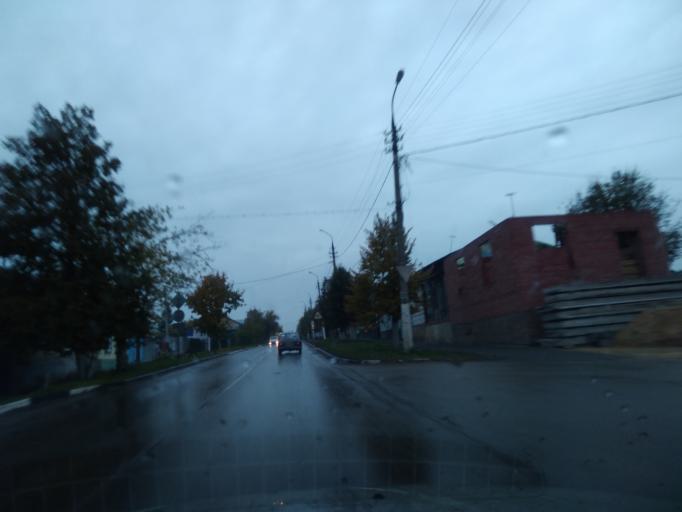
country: RU
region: Tula
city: Yefremov
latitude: 53.1386
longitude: 38.1143
